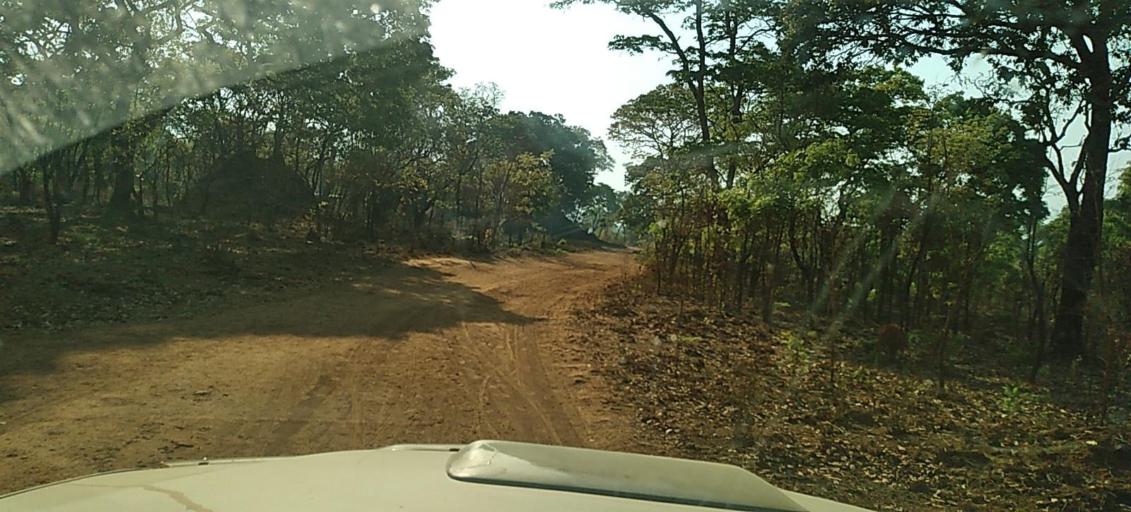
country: ZM
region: North-Western
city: Kasempa
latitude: -13.1852
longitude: 25.9616
